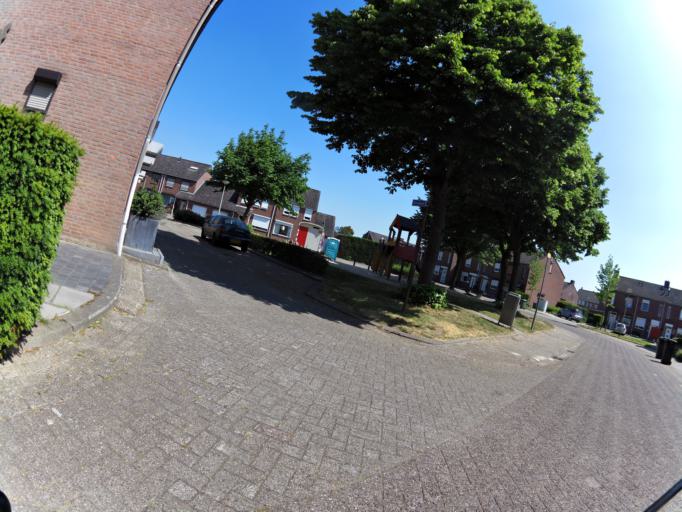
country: NL
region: Limburg
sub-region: Gemeente Kerkrade
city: Kerkrade
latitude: 50.9178
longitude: 6.0455
